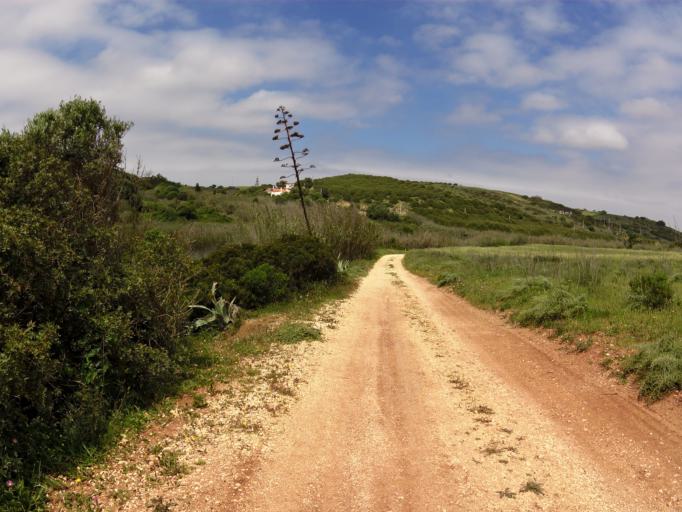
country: PT
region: Faro
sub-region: Vila do Bispo
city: Vila do Bispo
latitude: 37.0725
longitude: -8.8728
